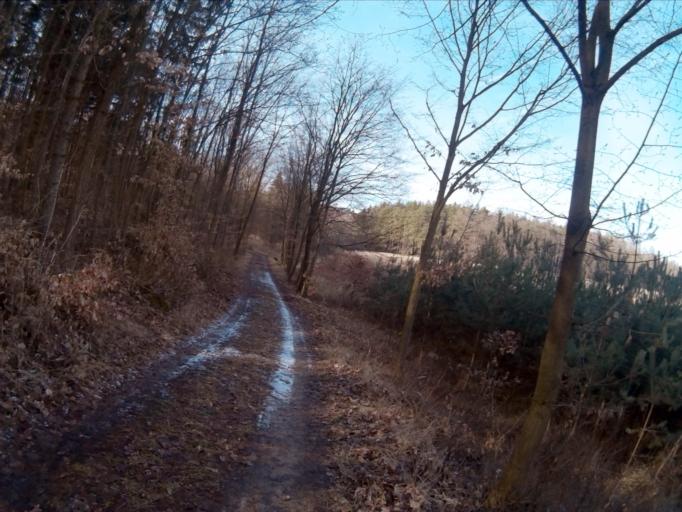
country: CZ
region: Vysocina
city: Mohelno
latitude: 49.1463
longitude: 16.1664
